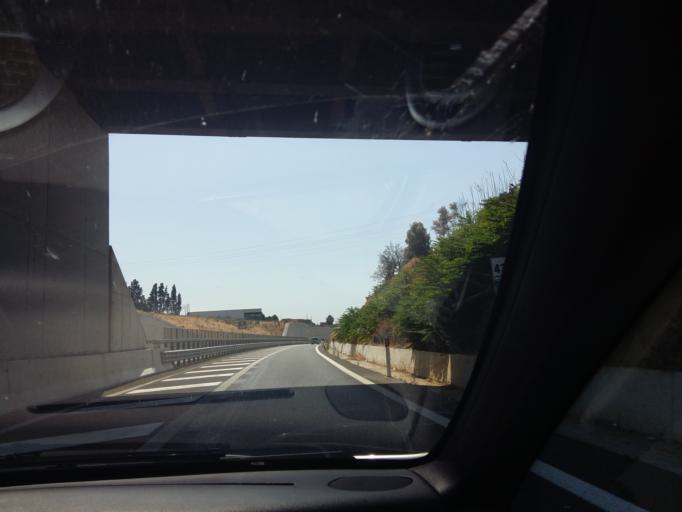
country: IT
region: Calabria
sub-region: Provincia di Reggio Calabria
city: Campo Calabro
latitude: 38.2182
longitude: 15.6477
